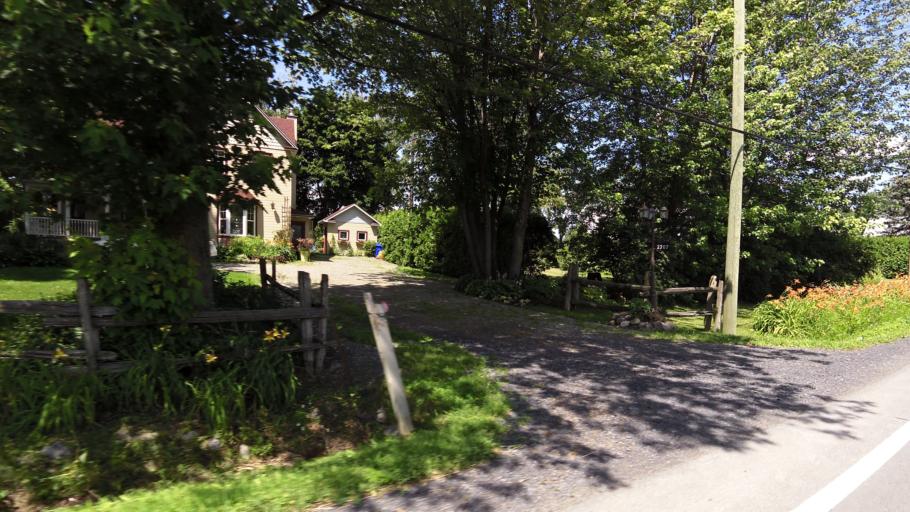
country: CA
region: Quebec
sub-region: Monteregie
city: Richelieu
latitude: 45.3939
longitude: -73.2505
